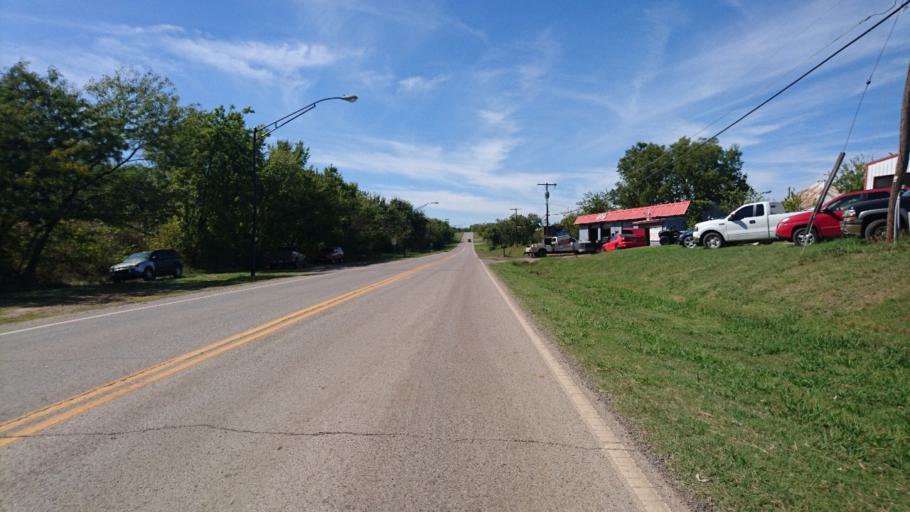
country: US
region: Oklahoma
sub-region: Lincoln County
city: Stroud
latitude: 35.7496
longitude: -96.6657
